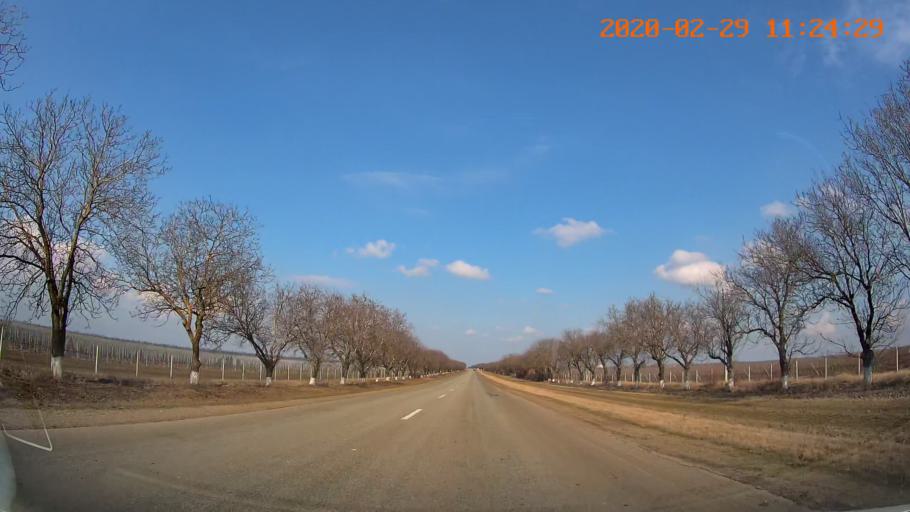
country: MD
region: Telenesti
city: Cocieri
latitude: 47.4245
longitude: 29.1544
